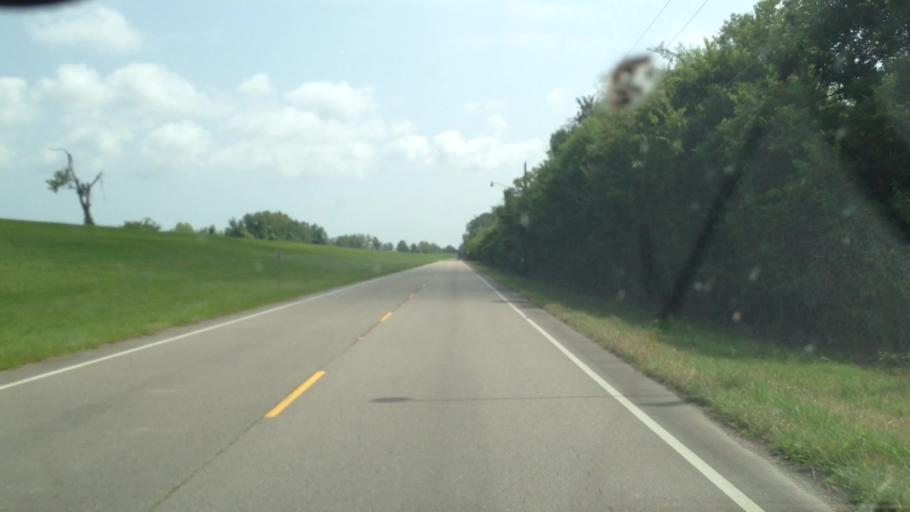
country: US
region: Louisiana
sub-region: Jefferson Parish
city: Bridge City
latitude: 29.9433
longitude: -90.1632
